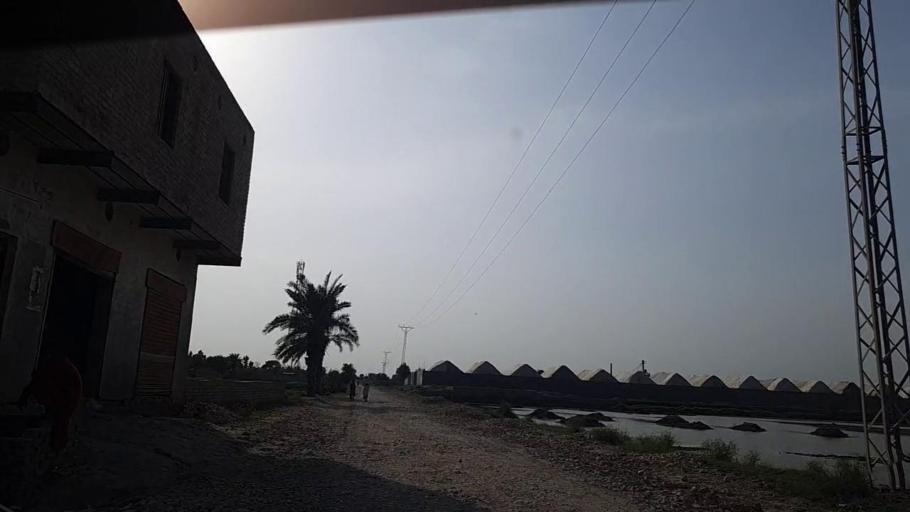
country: PK
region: Sindh
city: Ghotki
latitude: 28.0157
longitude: 69.2954
